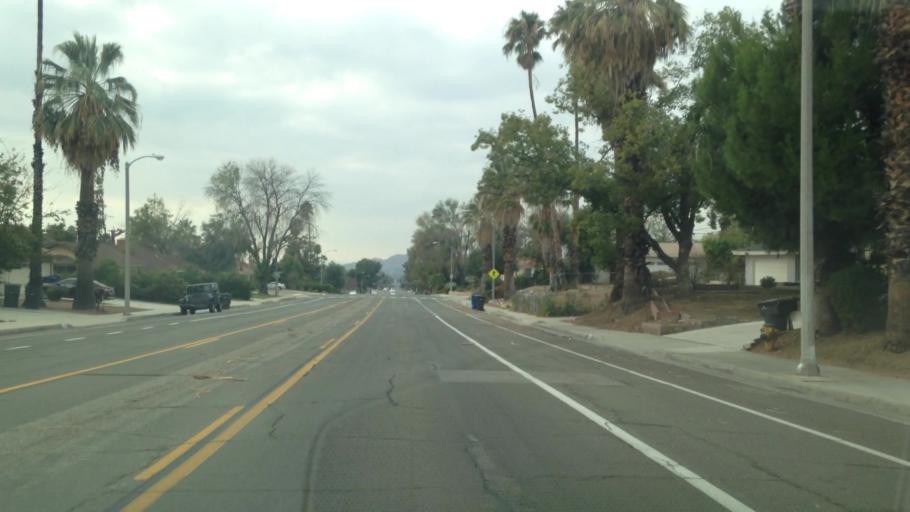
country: US
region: California
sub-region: Riverside County
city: Highgrove
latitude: 33.9830
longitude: -117.3191
